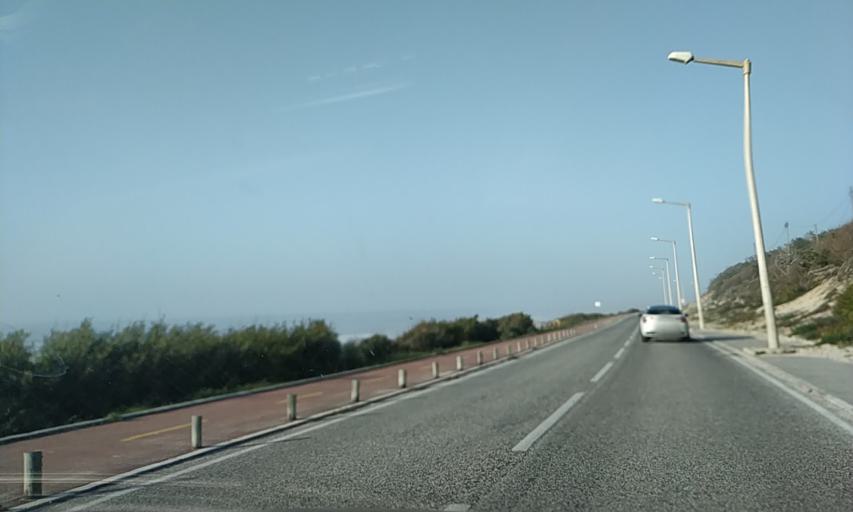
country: PT
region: Leiria
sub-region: Marinha Grande
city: Marinha Grande
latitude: 39.7714
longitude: -9.0242
